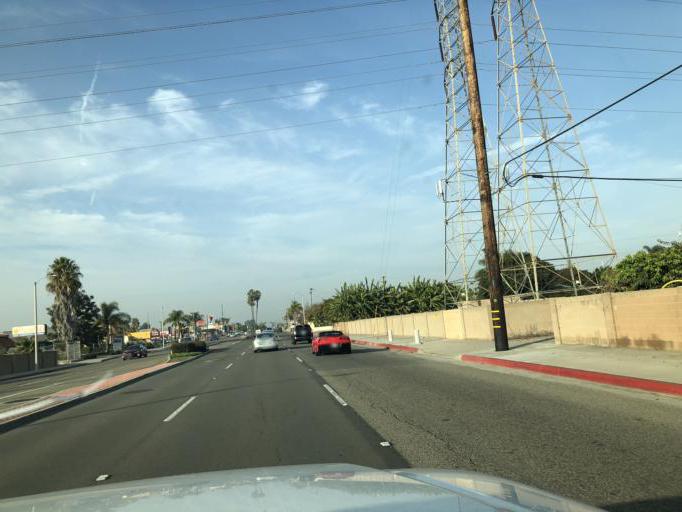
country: US
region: California
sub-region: Orange County
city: Fountain Valley
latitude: 33.6831
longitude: -117.9539
